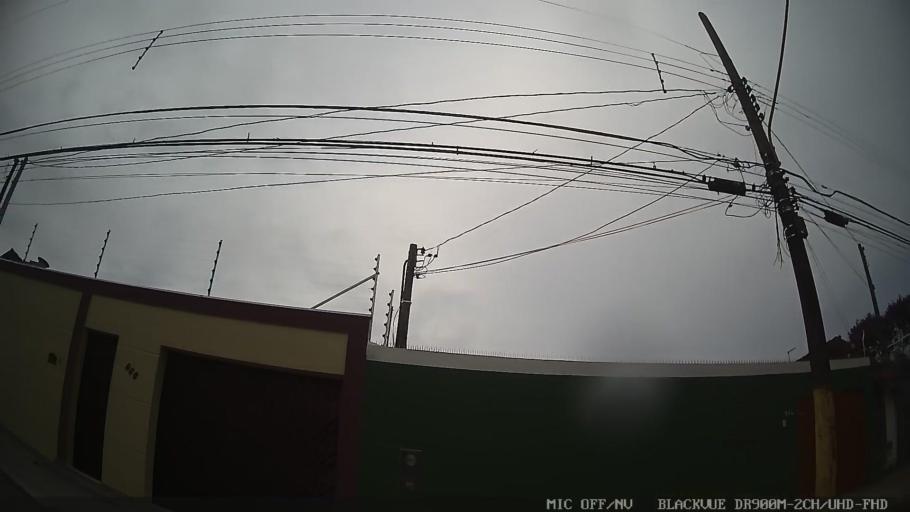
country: BR
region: Sao Paulo
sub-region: Guaruja
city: Guaruja
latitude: -23.9773
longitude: -46.2284
